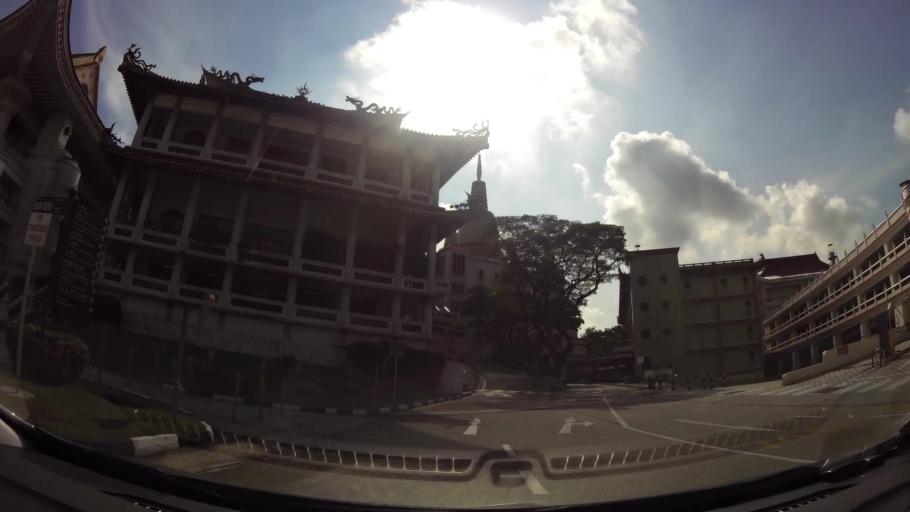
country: SG
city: Singapore
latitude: 1.3609
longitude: 103.8353
